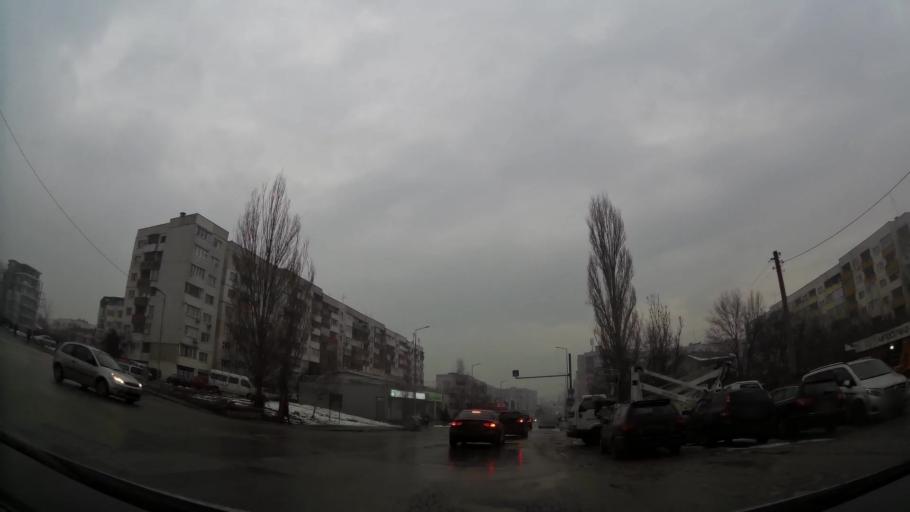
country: BG
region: Sofia-Capital
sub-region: Stolichna Obshtina
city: Sofia
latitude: 42.6849
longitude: 23.2559
